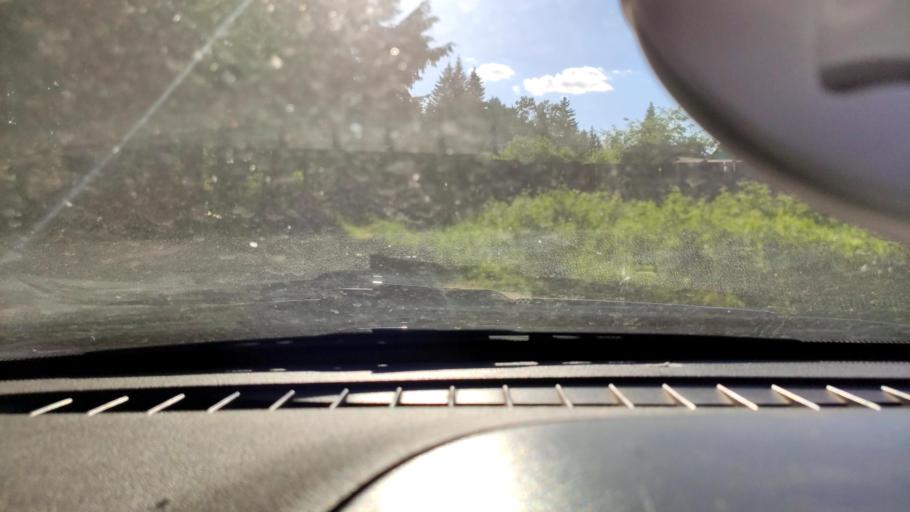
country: RU
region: Perm
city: Bershet'
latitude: 57.6983
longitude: 56.4112
